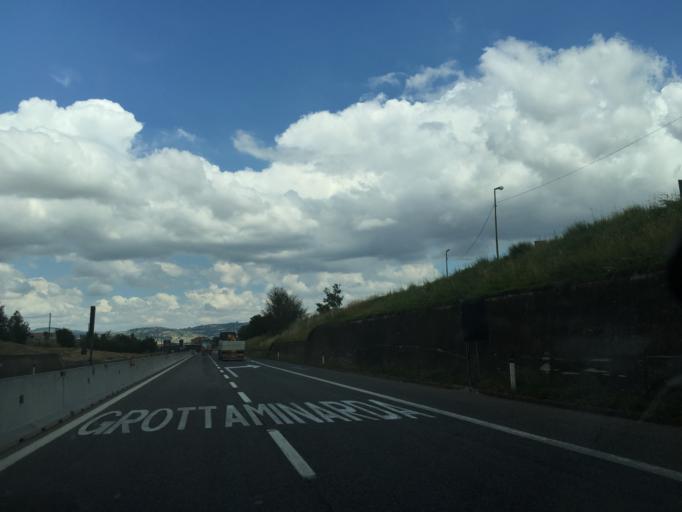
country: IT
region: Campania
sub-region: Provincia di Avellino
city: Grottaminarda
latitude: 41.0635
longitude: 15.0580
